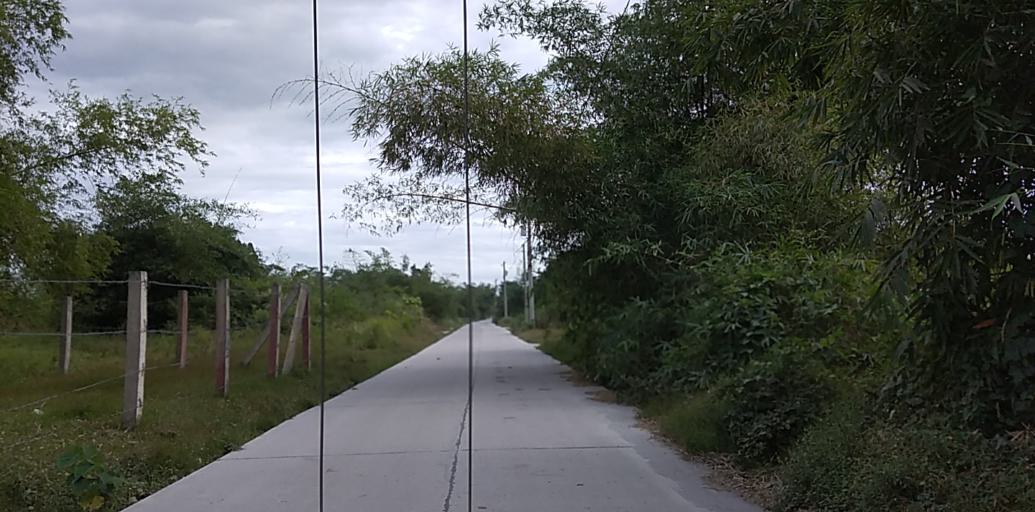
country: PH
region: Central Luzon
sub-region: Province of Pampanga
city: Pulung Santol
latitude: 15.0574
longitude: 120.5568
